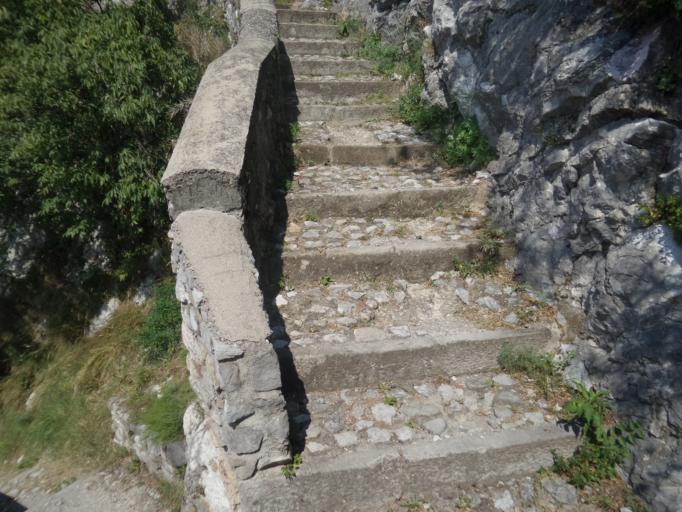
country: IT
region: Lombardy
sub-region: Provincia di Lecco
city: Vercurago
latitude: 45.8150
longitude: 9.4268
